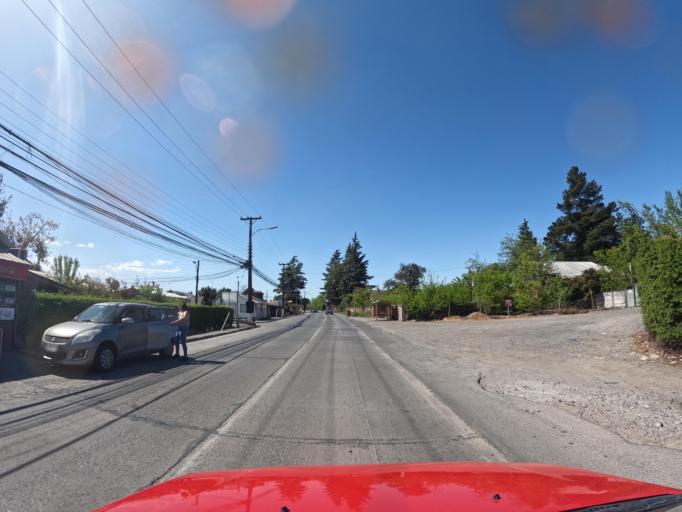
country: CL
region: Maule
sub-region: Provincia de Curico
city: Molina
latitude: -35.0758
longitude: -71.2583
